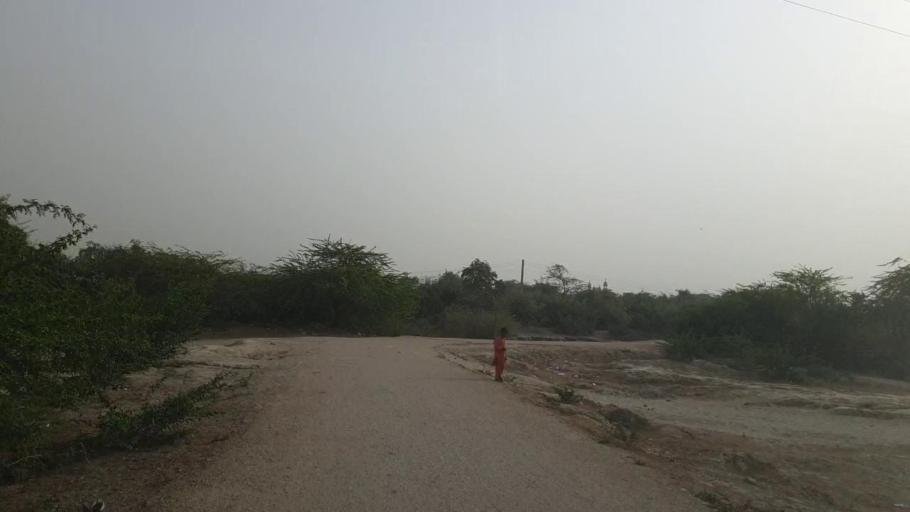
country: PK
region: Sindh
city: Kunri
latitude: 25.0663
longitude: 69.4585
